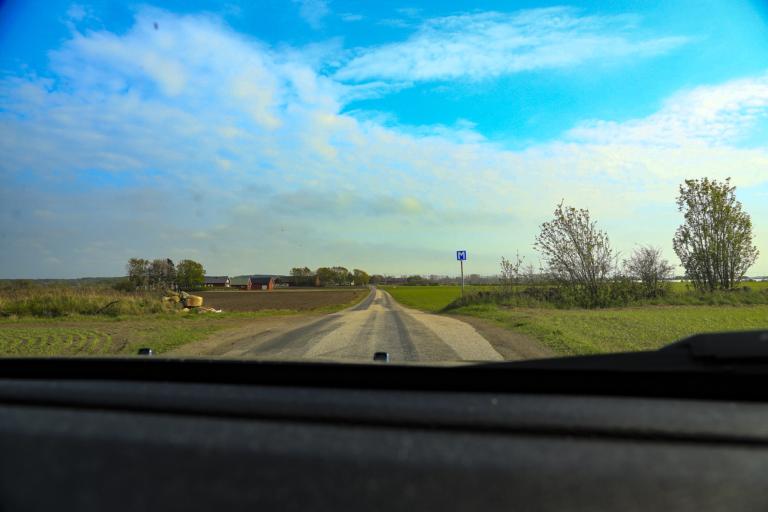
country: SE
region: Halland
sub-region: Varbergs Kommun
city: Traslovslage
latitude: 57.0972
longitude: 12.2998
